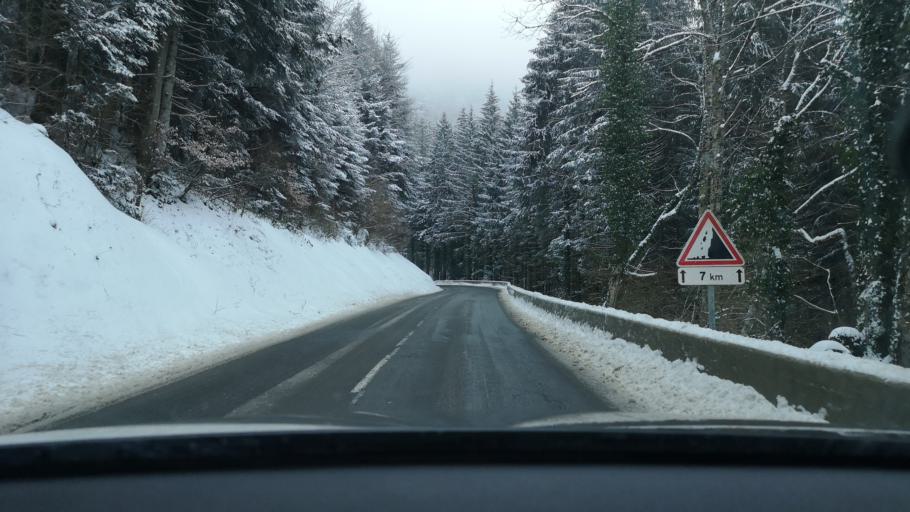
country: FR
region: Rhone-Alpes
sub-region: Departement de l'Ain
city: Arbent
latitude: 46.2540
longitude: 5.7038
